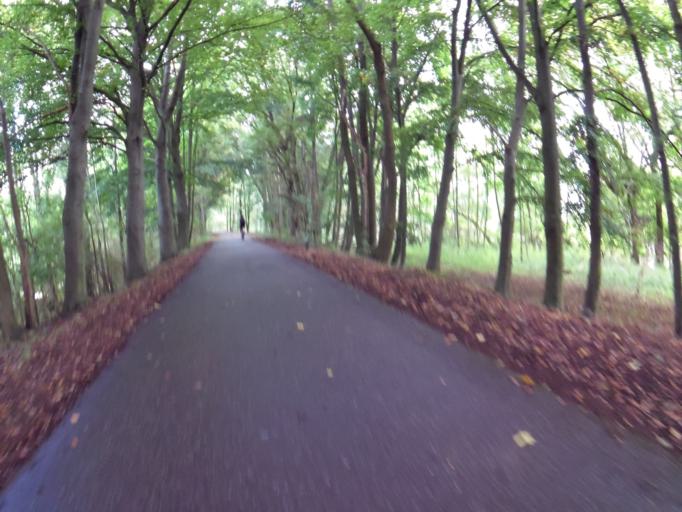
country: BE
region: Flanders
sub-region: Provincie Limburg
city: Lanaken
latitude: 50.8977
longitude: 5.6908
